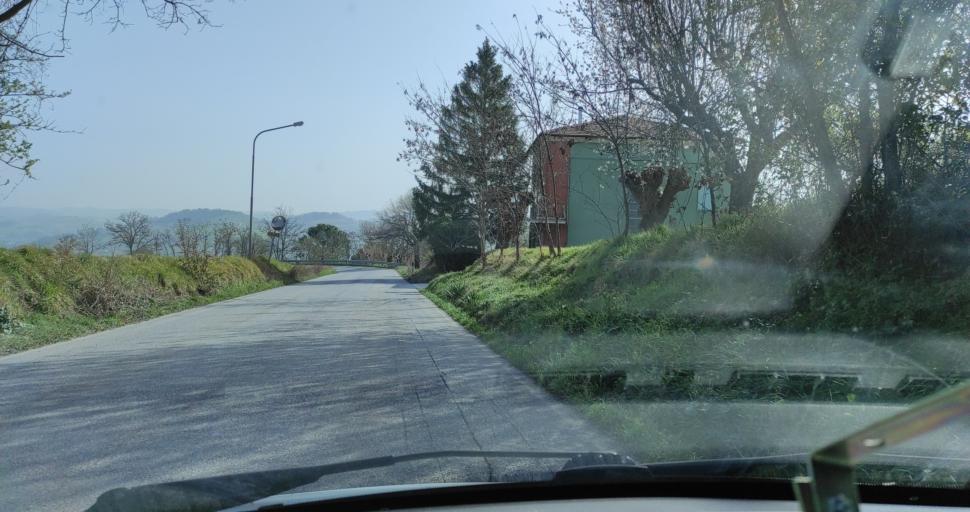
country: IT
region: The Marches
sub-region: Provincia di Macerata
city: Loro Piceno
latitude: 43.1619
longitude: 13.4255
